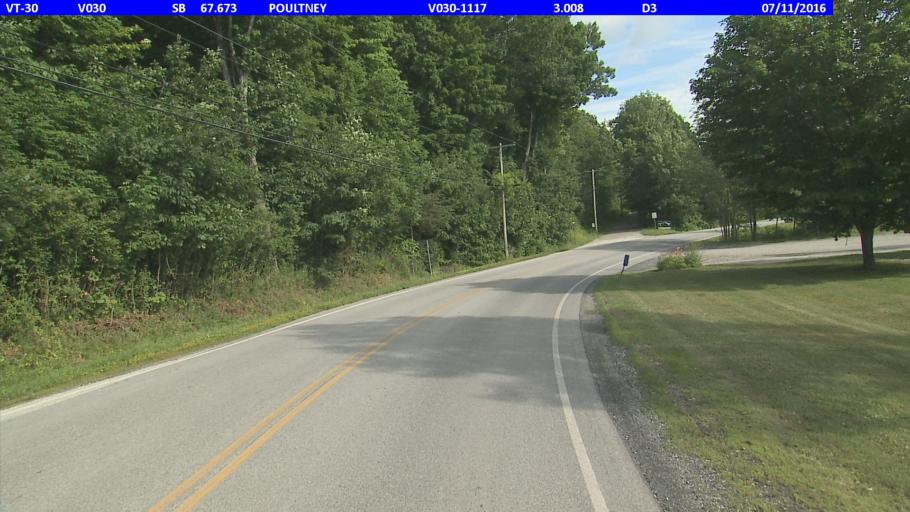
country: US
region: Vermont
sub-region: Rutland County
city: Poultney
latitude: 43.5049
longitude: -73.2100
